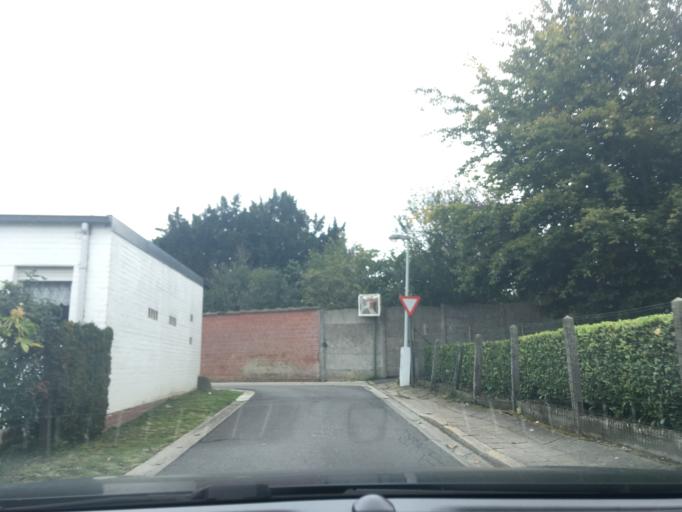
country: BE
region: Flanders
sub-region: Provincie West-Vlaanderen
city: Moorslede
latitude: 50.8924
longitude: 3.0640
